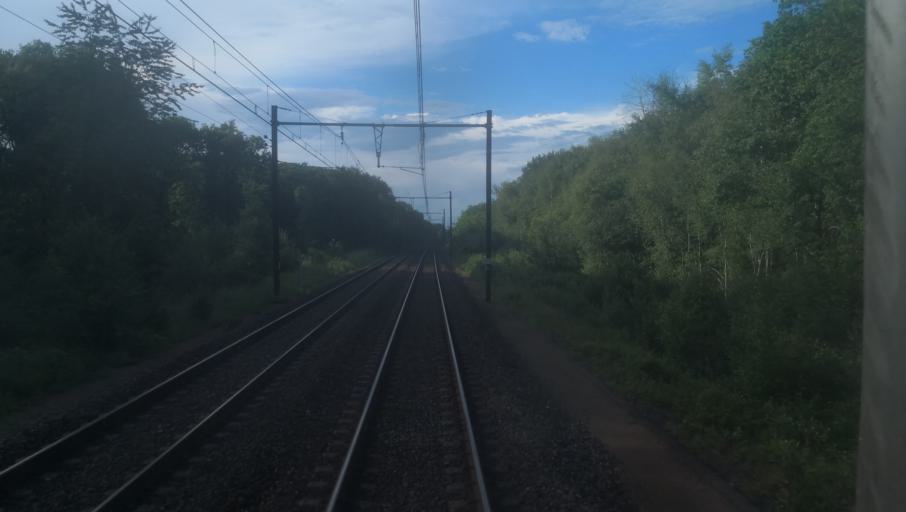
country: FR
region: Centre
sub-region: Departement du Loir-et-Cher
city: Salbris
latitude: 47.4480
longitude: 2.0426
